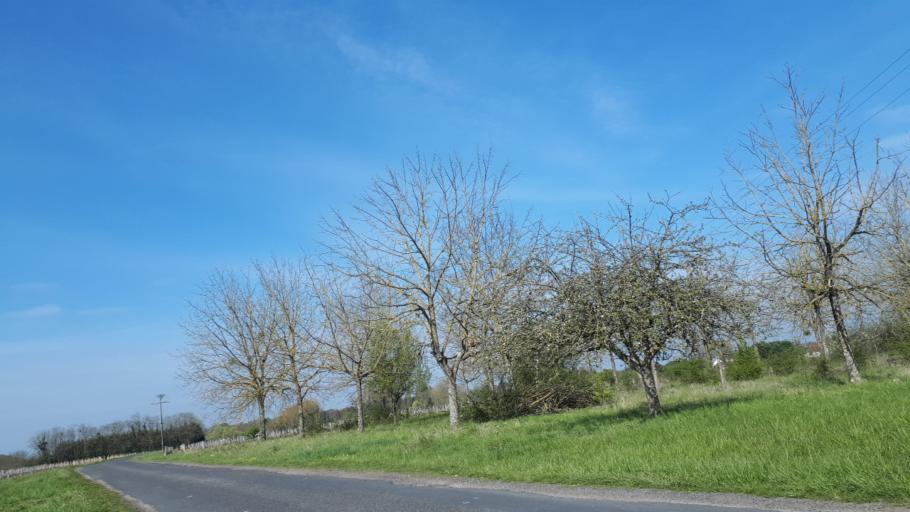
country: FR
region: Centre
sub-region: Departement du Loir-et-Cher
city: Contres
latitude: 47.3879
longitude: 1.3860
